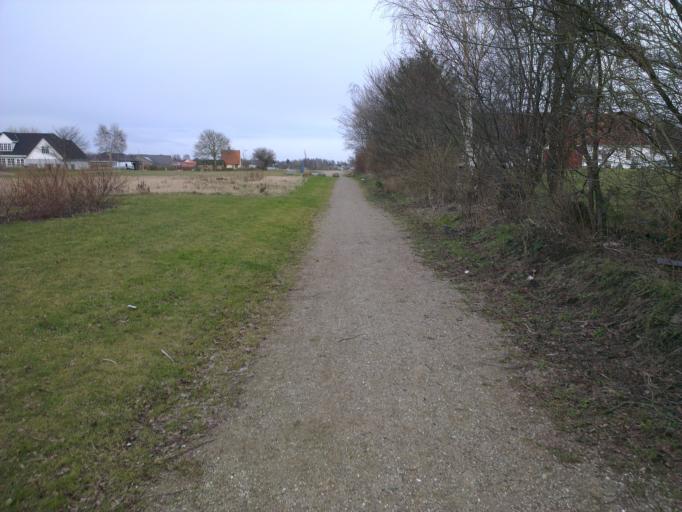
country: DK
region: Capital Region
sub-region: Frederikssund Kommune
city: Frederikssund
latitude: 55.8161
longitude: 12.0751
